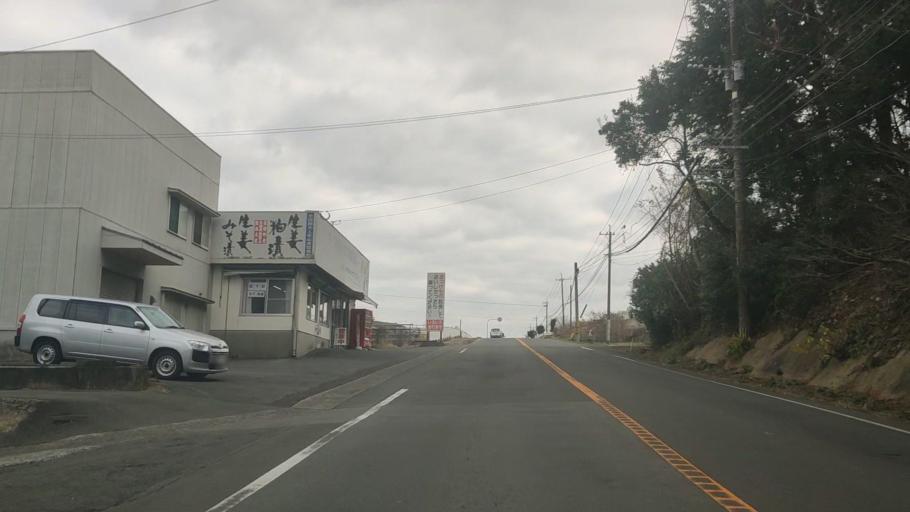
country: JP
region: Nagasaki
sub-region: Isahaya-shi
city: Isahaya
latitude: 32.7843
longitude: 130.0399
